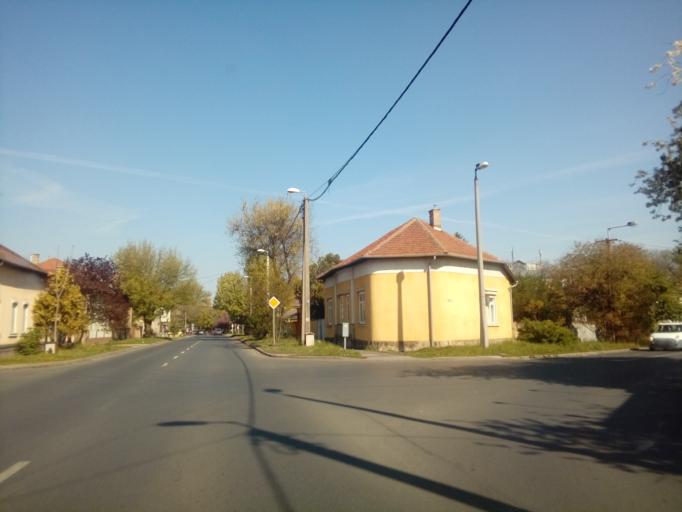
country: HU
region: Szabolcs-Szatmar-Bereg
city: Nyiregyhaza
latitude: 47.9479
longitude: 21.7323
